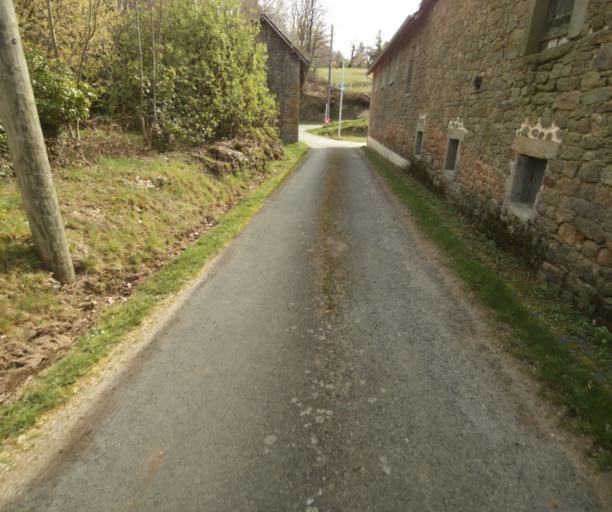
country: FR
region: Limousin
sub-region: Departement de la Correze
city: Correze
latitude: 45.4036
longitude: 1.8250
